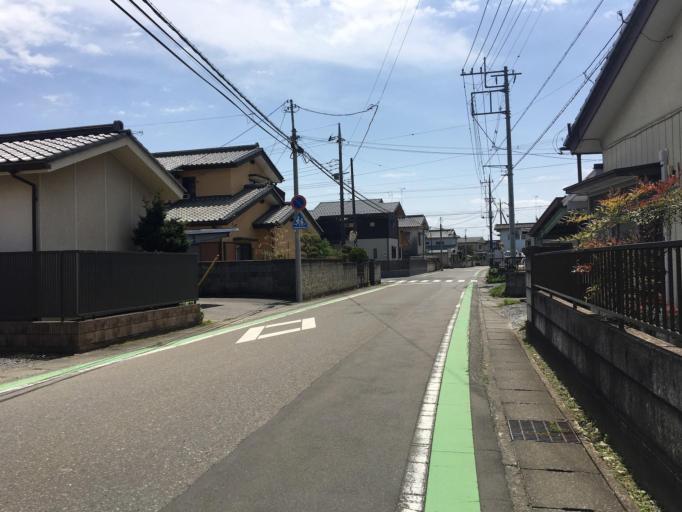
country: JP
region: Tochigi
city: Mibu
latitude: 36.4328
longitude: 139.8000
